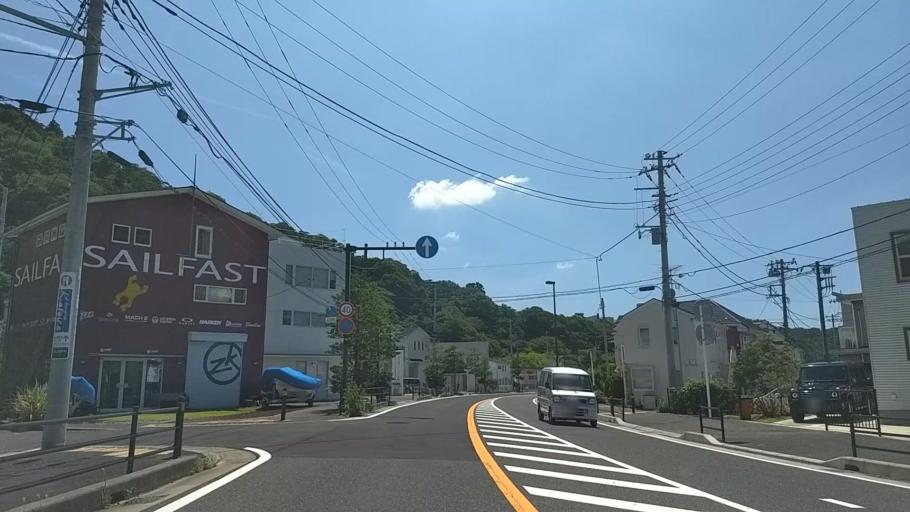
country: JP
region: Kanagawa
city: Hayama
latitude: 35.2834
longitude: 139.5887
